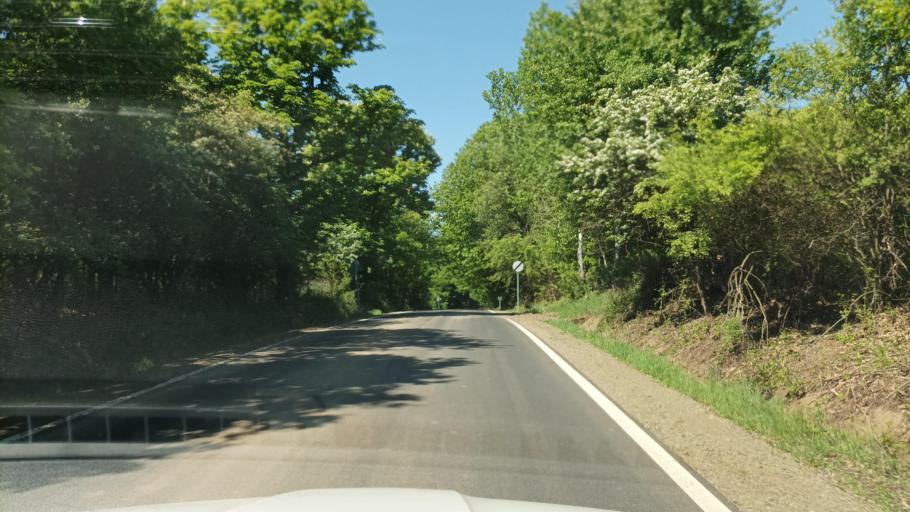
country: HU
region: Pest
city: Acsa
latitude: 47.7847
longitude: 19.4316
